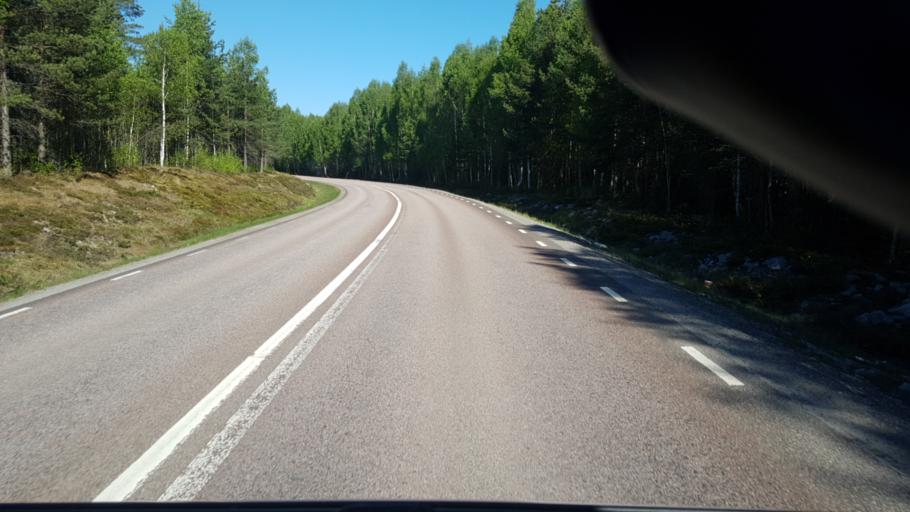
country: SE
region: Vaermland
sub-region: Eda Kommun
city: Amotfors
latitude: 59.6763
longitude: 12.4492
